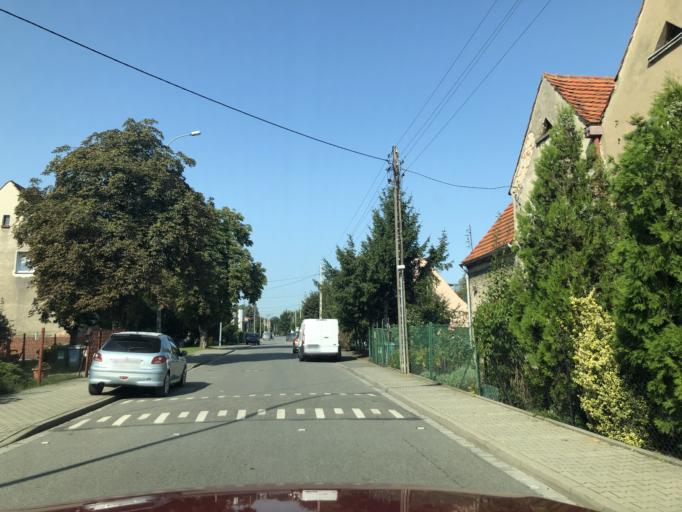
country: PL
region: Lower Silesian Voivodeship
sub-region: Powiat wroclawski
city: Smolec
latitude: 51.1585
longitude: 16.9041
